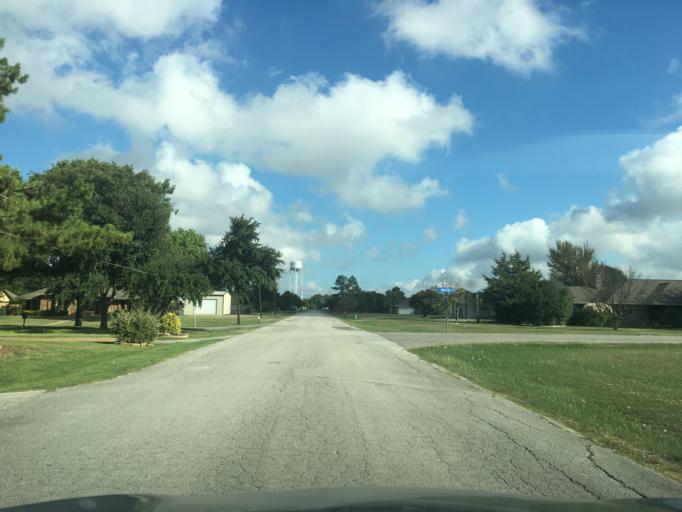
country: US
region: Texas
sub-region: Dallas County
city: Sachse
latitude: 32.9694
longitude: -96.5917
